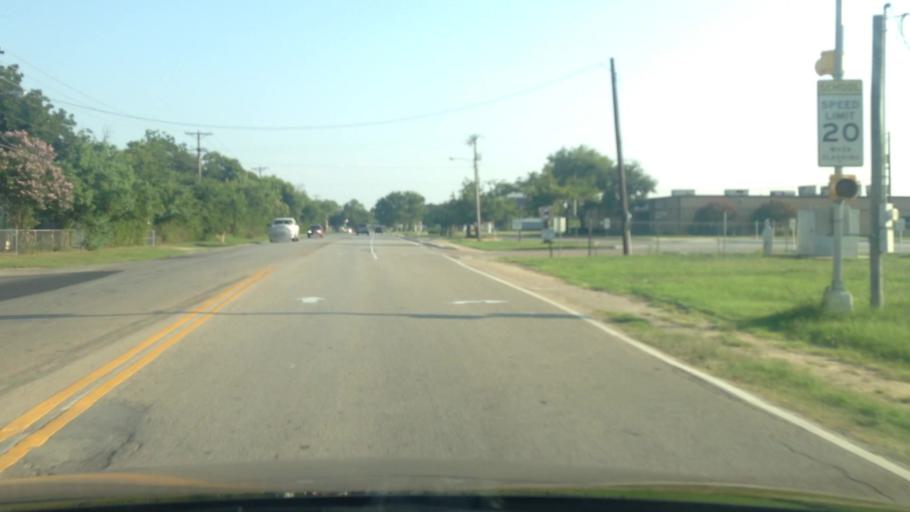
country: US
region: Texas
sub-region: Tarrant County
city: Everman
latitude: 32.6348
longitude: -97.2700
